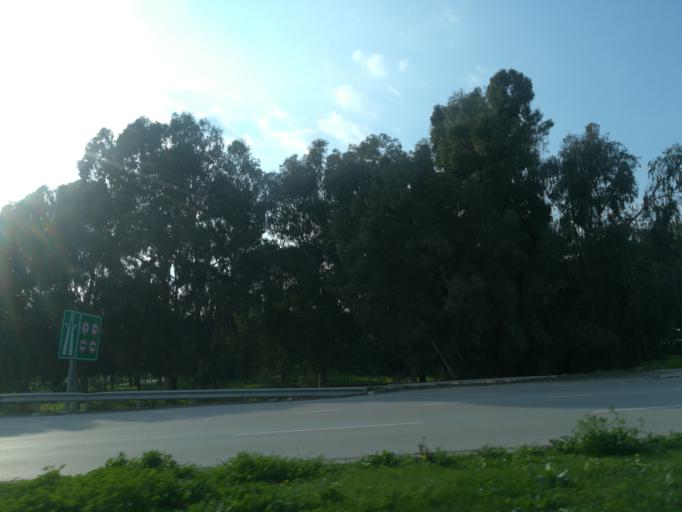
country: TR
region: Adana
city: Adana
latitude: 37.0270
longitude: 35.3445
